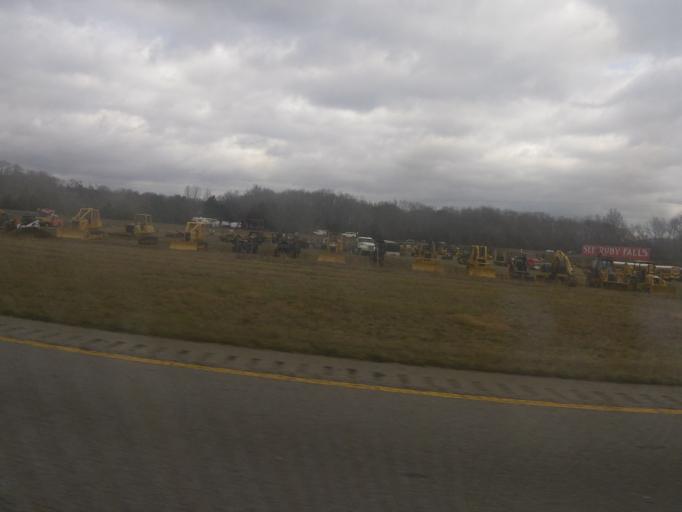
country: US
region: Tennessee
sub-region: Marion County
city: Jasper
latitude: 35.0435
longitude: -85.6076
